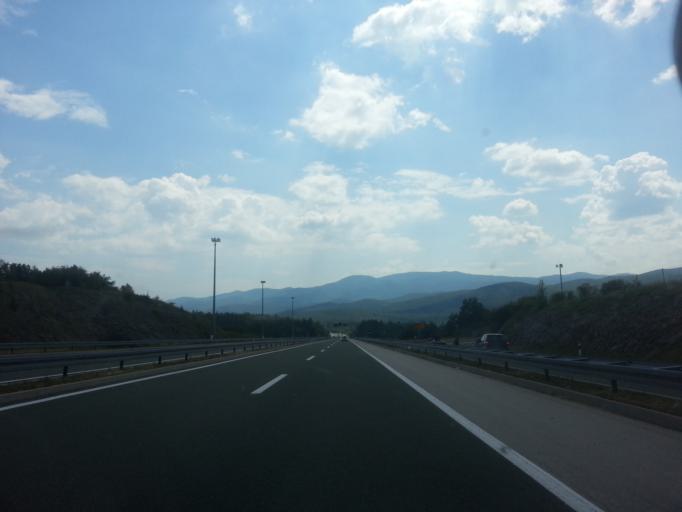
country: HR
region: Primorsko-Goranska
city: Klana
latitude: 45.4735
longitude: 14.2754
